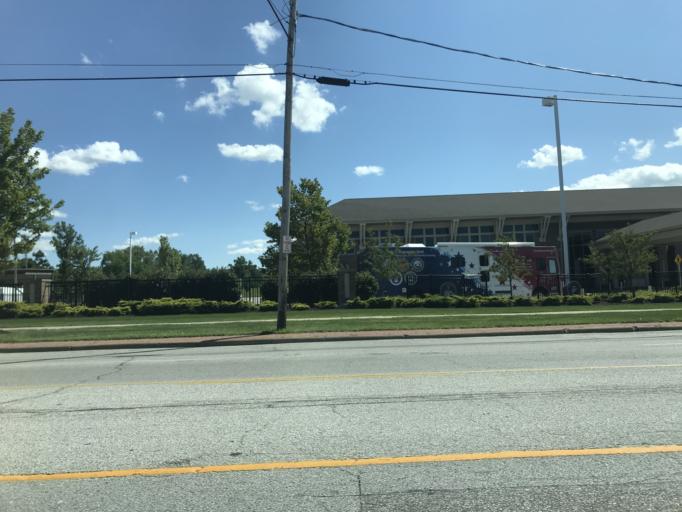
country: US
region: Ohio
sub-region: Cuyahoga County
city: Brooklyn
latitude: 41.4187
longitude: -81.7449
